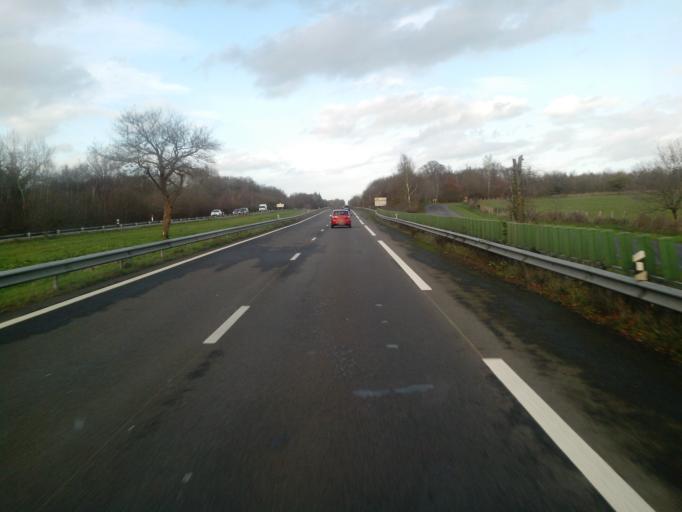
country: FR
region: Brittany
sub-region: Departement d'Ille-et-Vilaine
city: Miniac-Morvan
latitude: 48.4823
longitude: -1.9087
